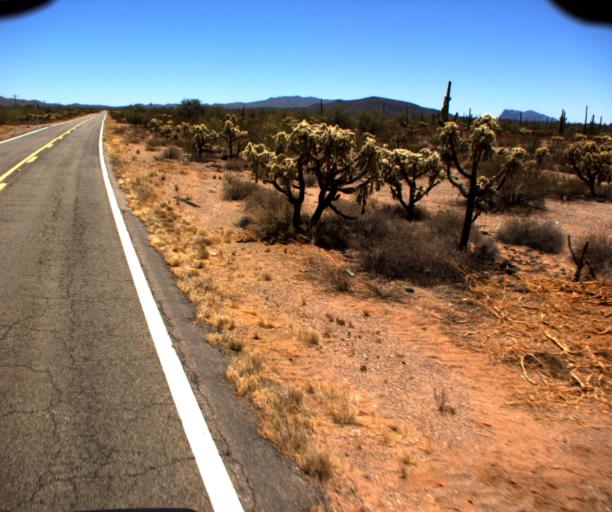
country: US
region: Arizona
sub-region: Pima County
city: Sells
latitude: 32.1831
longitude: -112.3027
